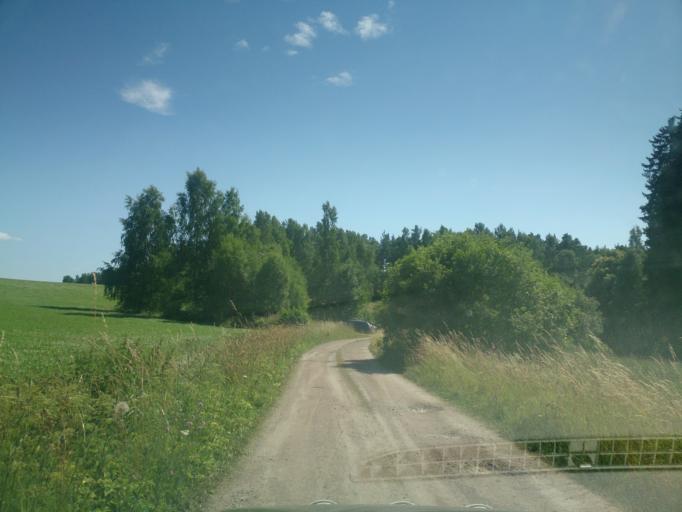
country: SE
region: OEstergoetland
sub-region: Atvidabergs Kommun
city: Atvidaberg
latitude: 58.2388
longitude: 15.9631
